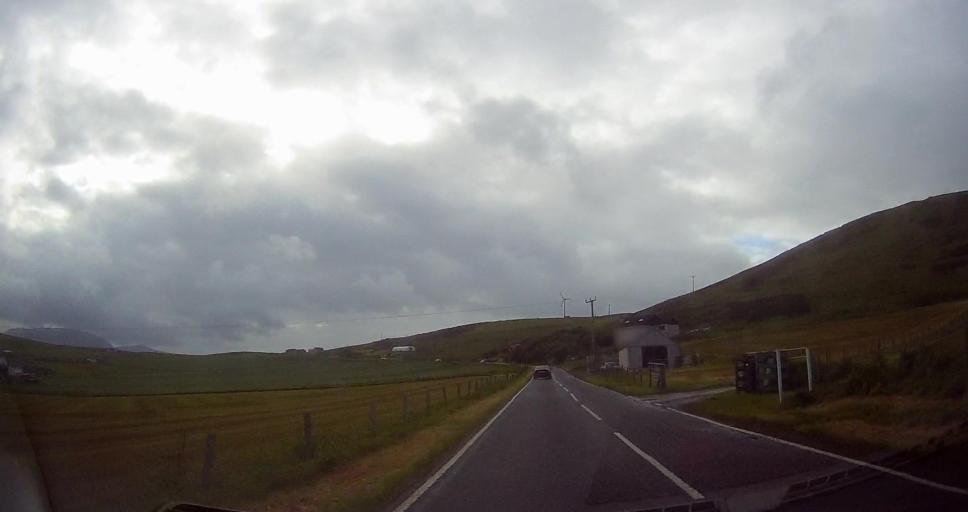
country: GB
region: Scotland
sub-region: Orkney Islands
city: Stromness
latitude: 58.9196
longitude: -3.1817
